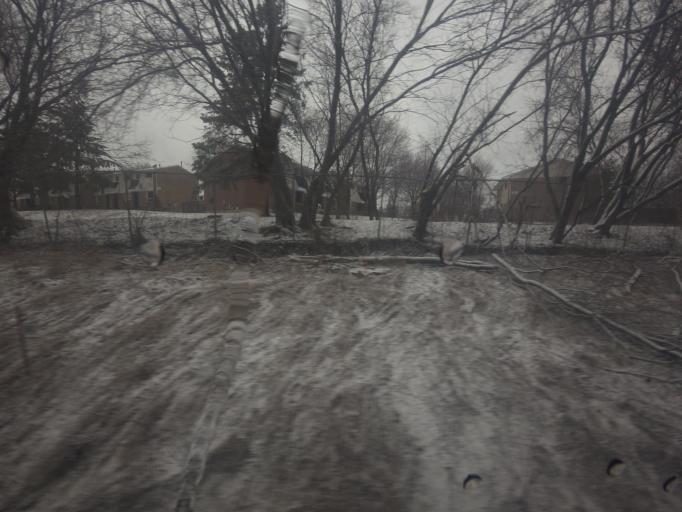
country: CA
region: Ontario
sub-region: Lanark County
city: Smiths Falls
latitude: 44.9003
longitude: -76.0098
